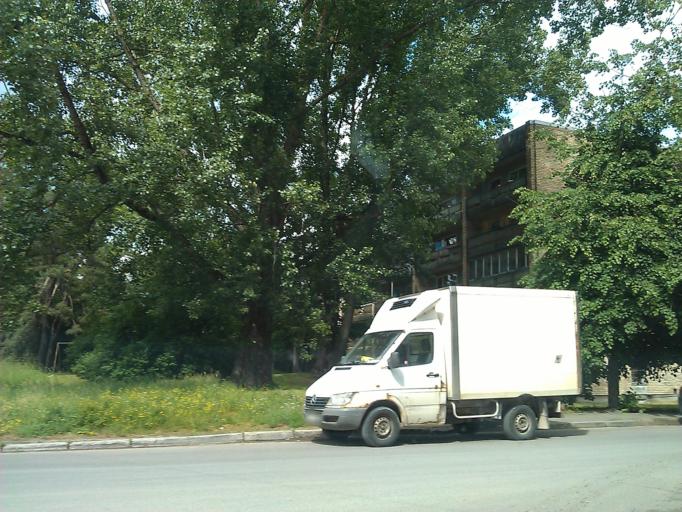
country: LV
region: Riga
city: Jaunciems
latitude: 56.9929
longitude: 24.2281
